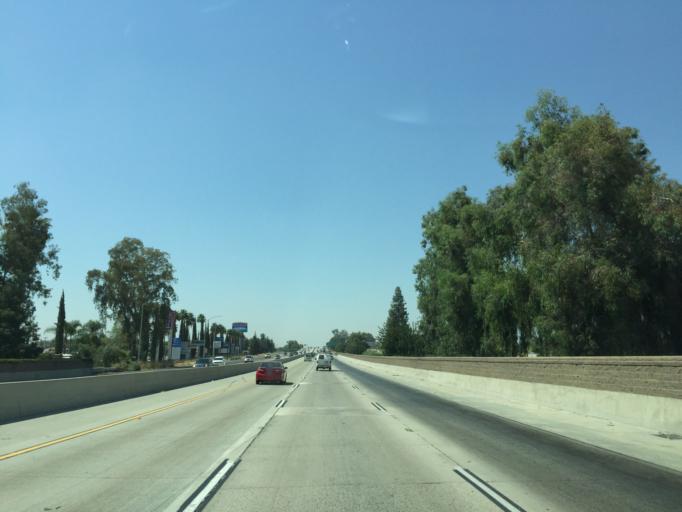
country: US
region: California
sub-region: Fresno County
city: Selma
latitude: 36.5698
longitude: -119.6221
